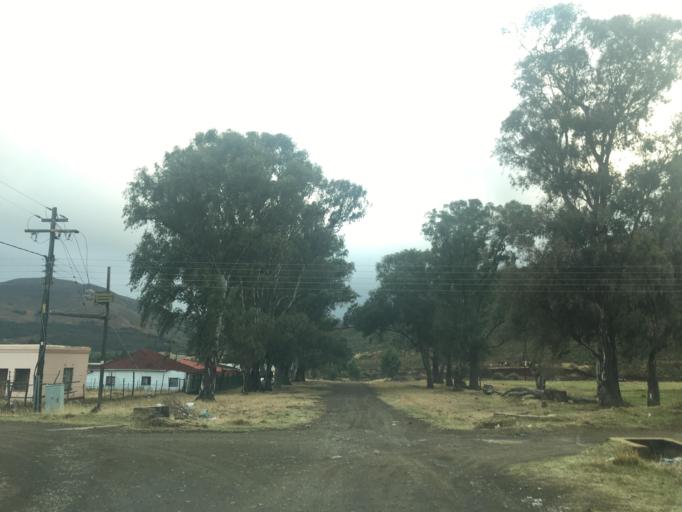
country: ZA
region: Eastern Cape
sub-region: Chris Hani District Municipality
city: Cala
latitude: -31.5211
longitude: 27.7009
